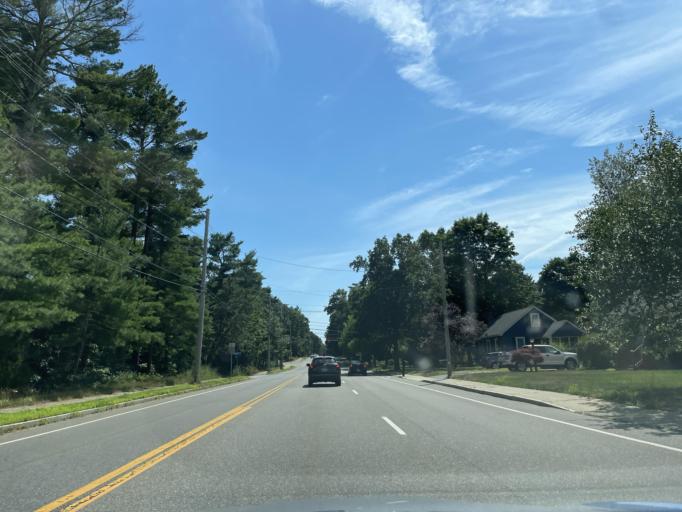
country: US
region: Massachusetts
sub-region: Norfolk County
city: Foxborough
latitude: 42.0909
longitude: -71.2263
